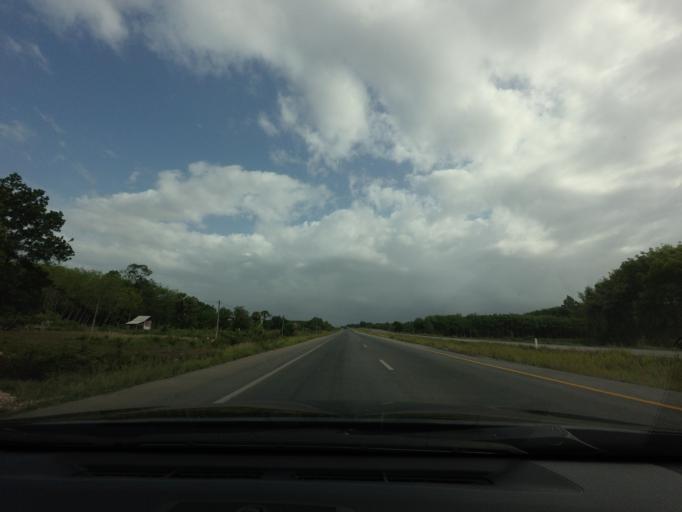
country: TH
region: Pattani
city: Mae Lan
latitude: 6.6666
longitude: 101.2346
